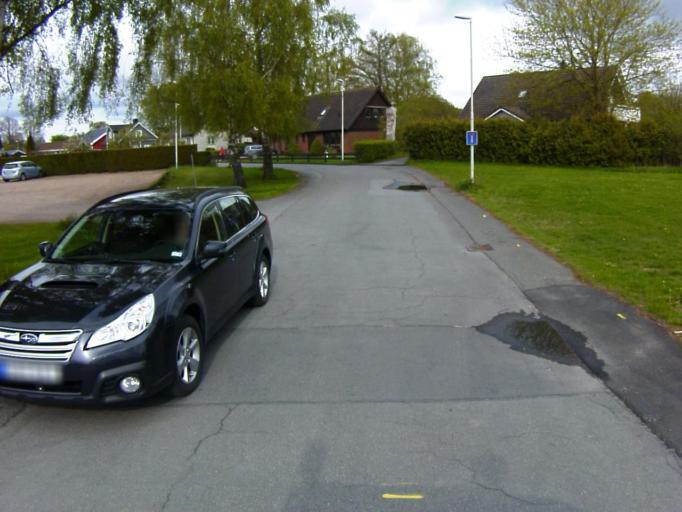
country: SE
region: Skane
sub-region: Kristianstads Kommun
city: Kristianstad
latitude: 56.0497
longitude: 14.1903
